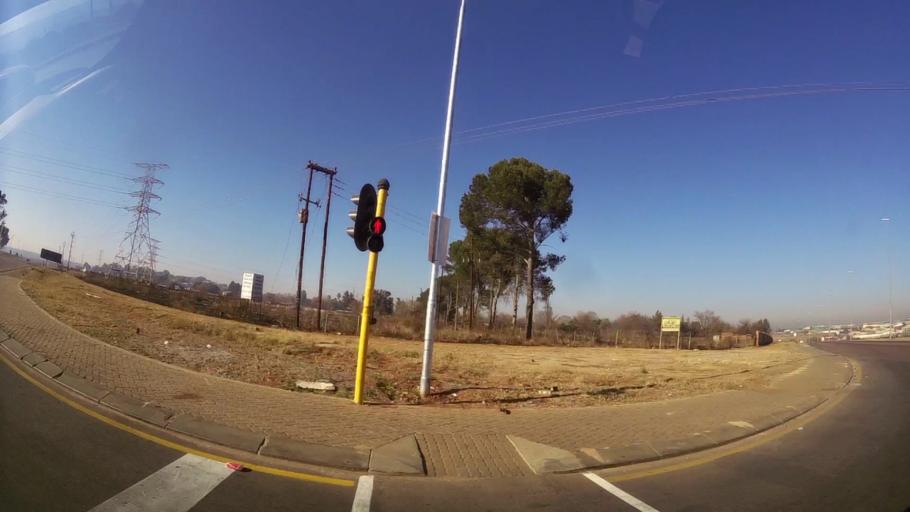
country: ZA
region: Gauteng
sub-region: City of Tshwane Metropolitan Municipality
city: Centurion
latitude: -25.8350
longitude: 28.1130
